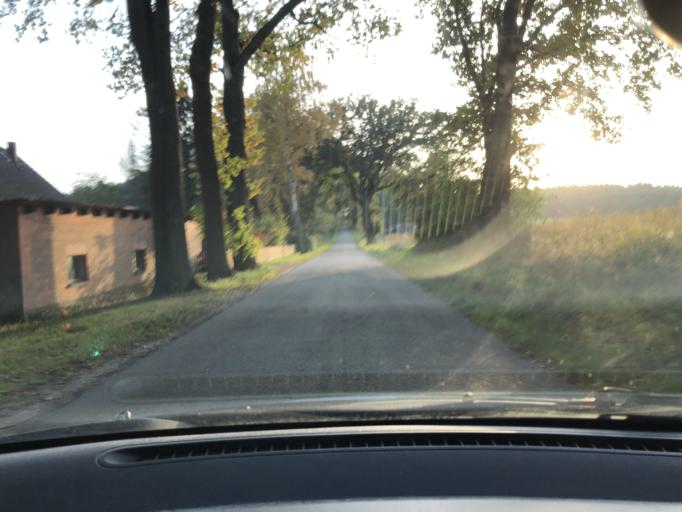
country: DE
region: Lower Saxony
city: Hitzacker
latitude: 53.1493
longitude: 10.9779
